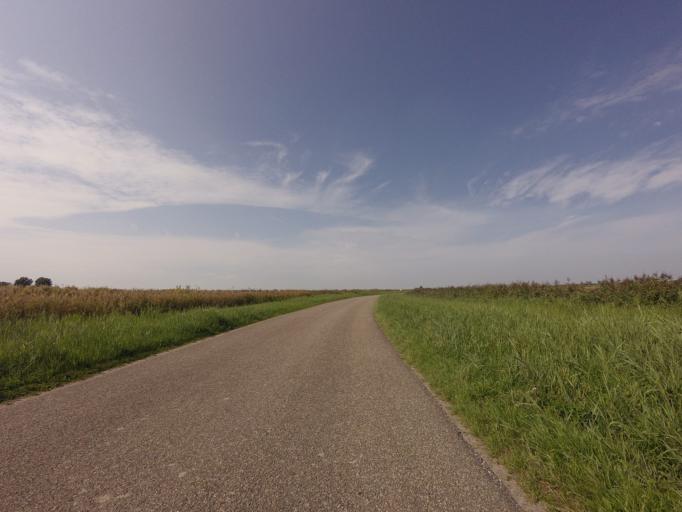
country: NL
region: Groningen
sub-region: Gemeente De Marne
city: Ulrum
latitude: 53.3428
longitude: 6.2832
